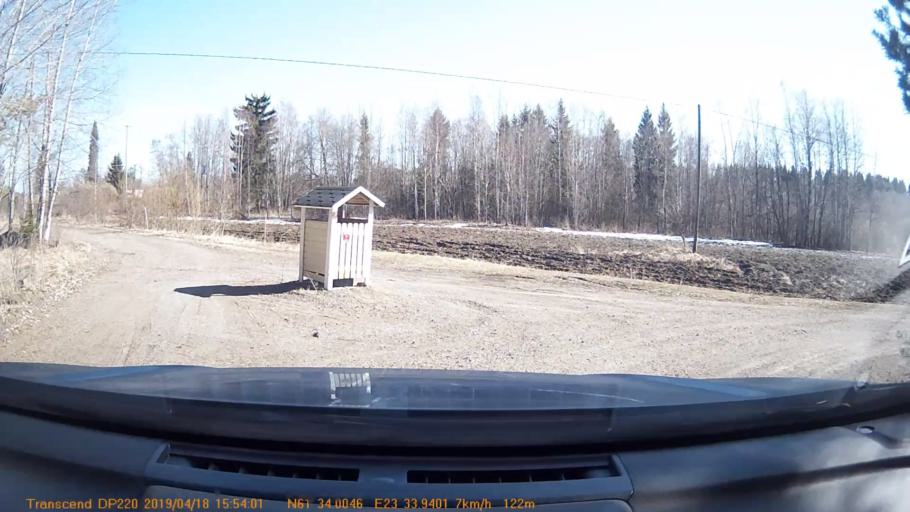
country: FI
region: Pirkanmaa
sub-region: Tampere
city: Yloejaervi
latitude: 61.5668
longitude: 23.5656
